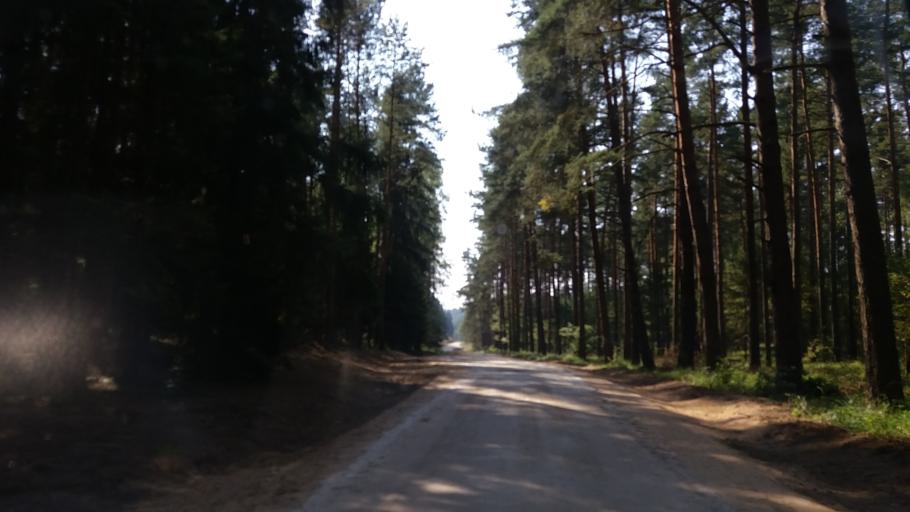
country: PL
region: West Pomeranian Voivodeship
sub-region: Powiat drawski
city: Kalisz Pomorski
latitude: 53.1131
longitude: 15.9311
